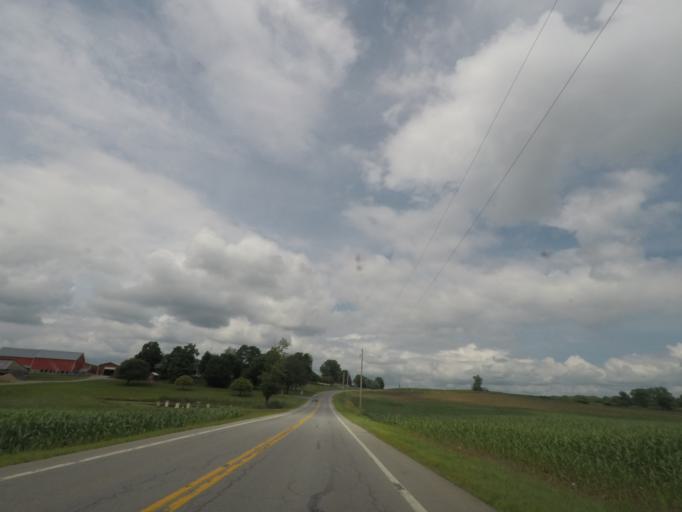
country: US
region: New York
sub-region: Saratoga County
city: Saratoga Springs
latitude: 43.0576
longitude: -73.6859
